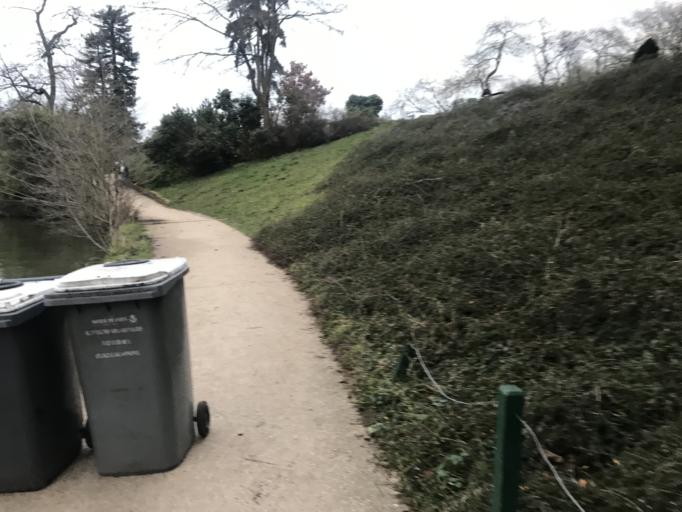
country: FR
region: Ile-de-France
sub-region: Departement des Hauts-de-Seine
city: Neuilly-sur-Seine
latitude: 48.8631
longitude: 2.2616
